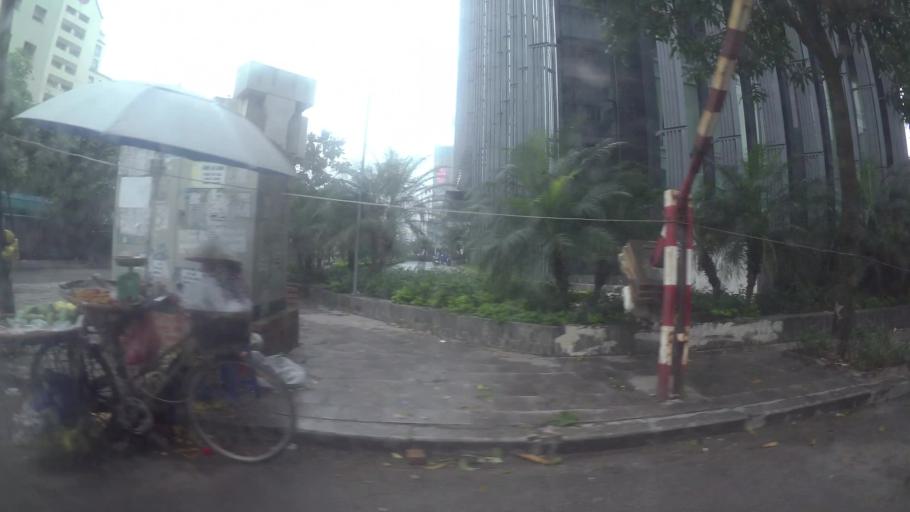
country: VN
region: Ha Noi
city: Cau Giay
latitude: 21.0233
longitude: 105.7889
